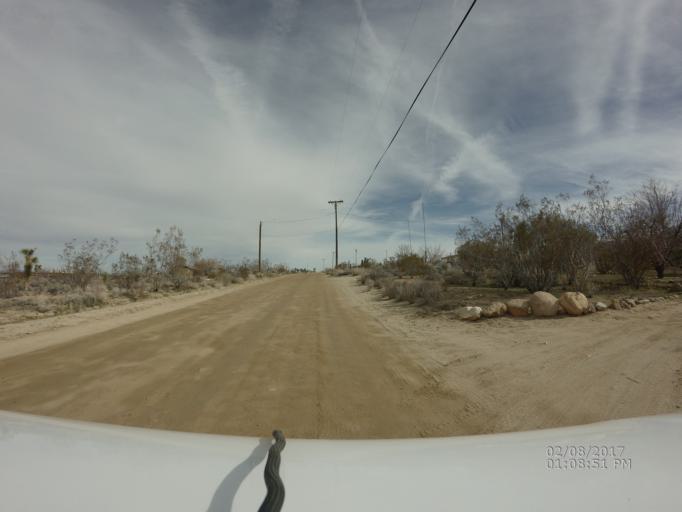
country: US
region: California
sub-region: Los Angeles County
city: Lake Los Angeles
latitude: 34.4762
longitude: -117.8260
